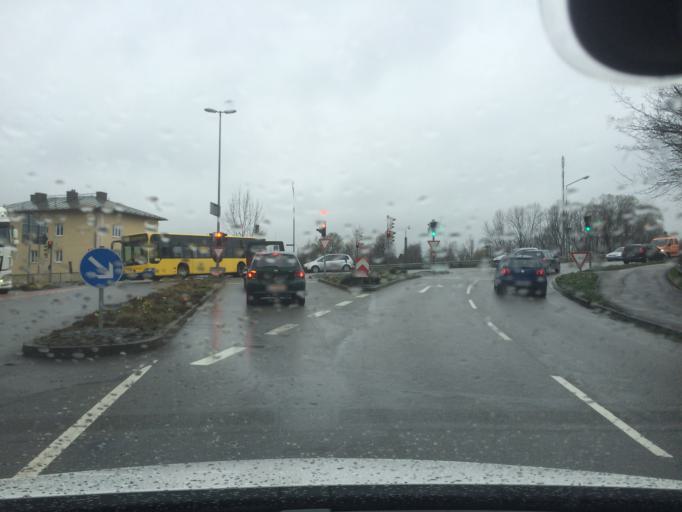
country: DE
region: Bavaria
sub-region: Upper Bavaria
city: Rosenheim
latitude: 47.8544
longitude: 12.1103
